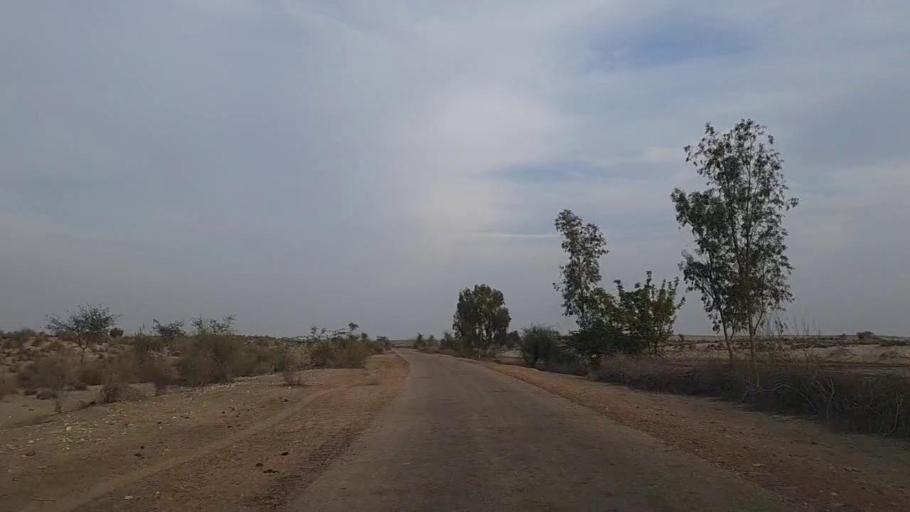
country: PK
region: Sindh
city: Daur
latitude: 26.4944
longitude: 68.5288
